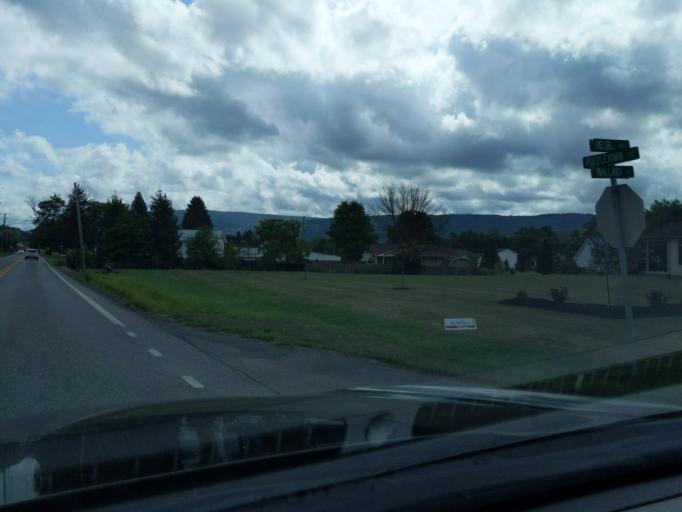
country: US
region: Pennsylvania
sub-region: Blair County
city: Duncansville
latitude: 40.3924
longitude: -78.4437
